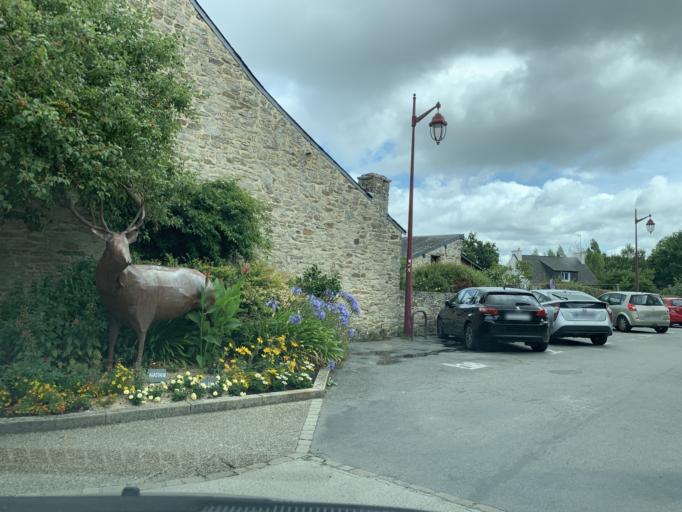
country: FR
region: Brittany
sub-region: Departement du Morbihan
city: Noyal-Muzillac
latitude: 47.5830
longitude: -2.4078
